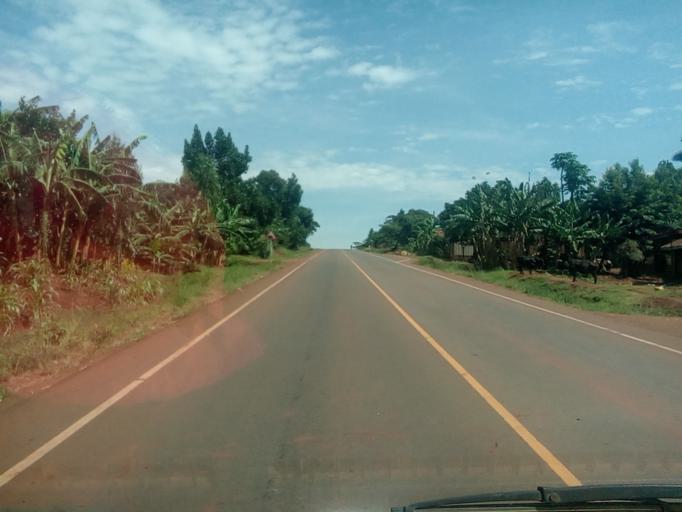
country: UG
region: Eastern Region
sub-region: Jinja District
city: Buwenge
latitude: 0.5816
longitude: 33.2048
